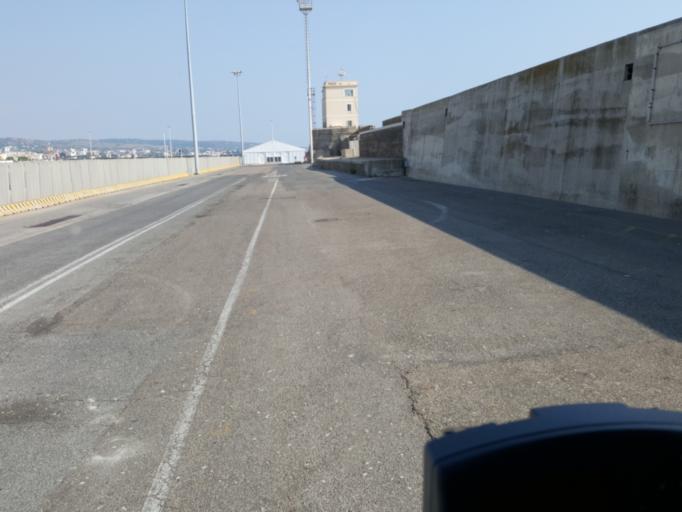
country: IT
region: Latium
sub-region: Citta metropolitana di Roma Capitale
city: Civitavecchia
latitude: 42.0919
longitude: 11.7837
